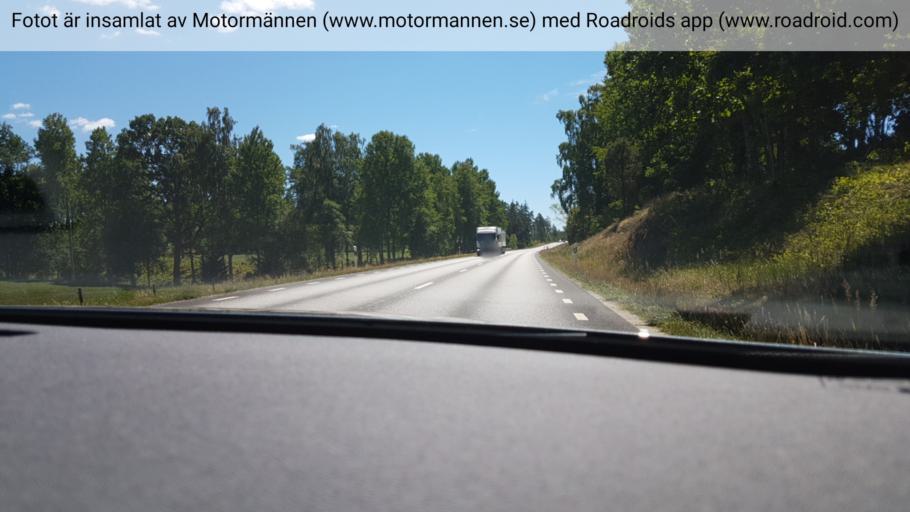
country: SE
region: Joenkoeping
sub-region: Gnosjo Kommun
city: Gnosjoe
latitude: 57.5372
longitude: 13.6883
